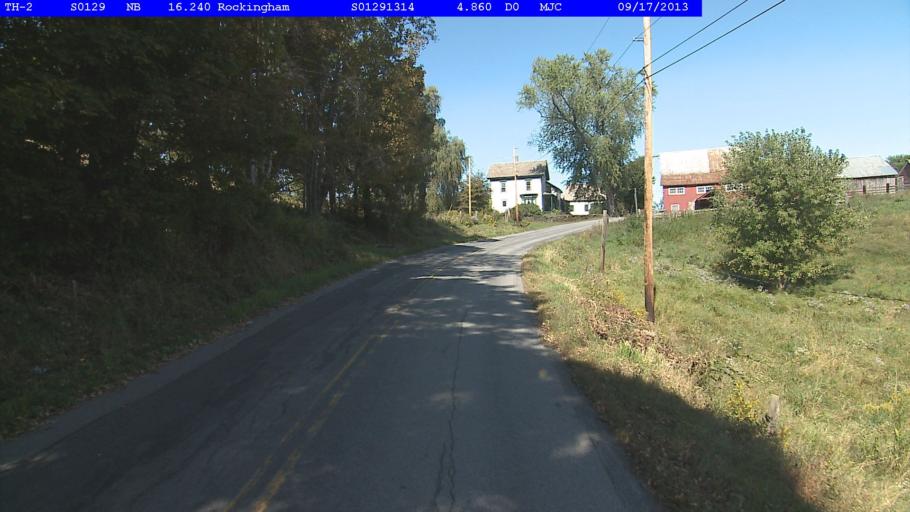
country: US
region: Vermont
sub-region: Windham County
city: Rockingham
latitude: 43.1866
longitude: -72.5127
